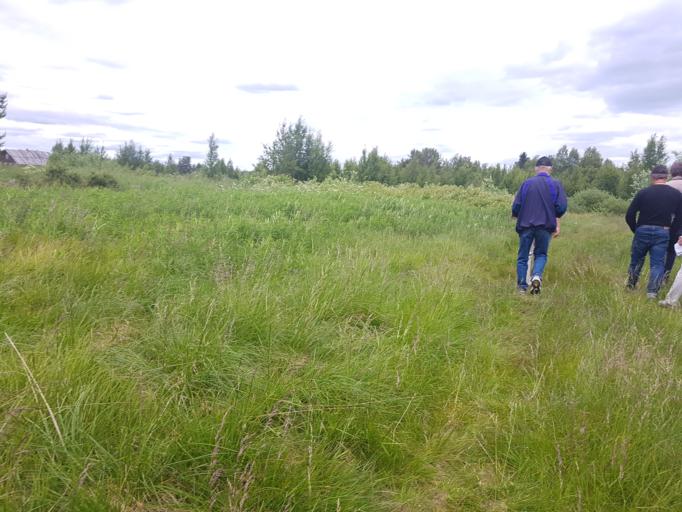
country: RU
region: Republic of Karelia
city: Yushkozero
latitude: 65.1639
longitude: 32.0126
